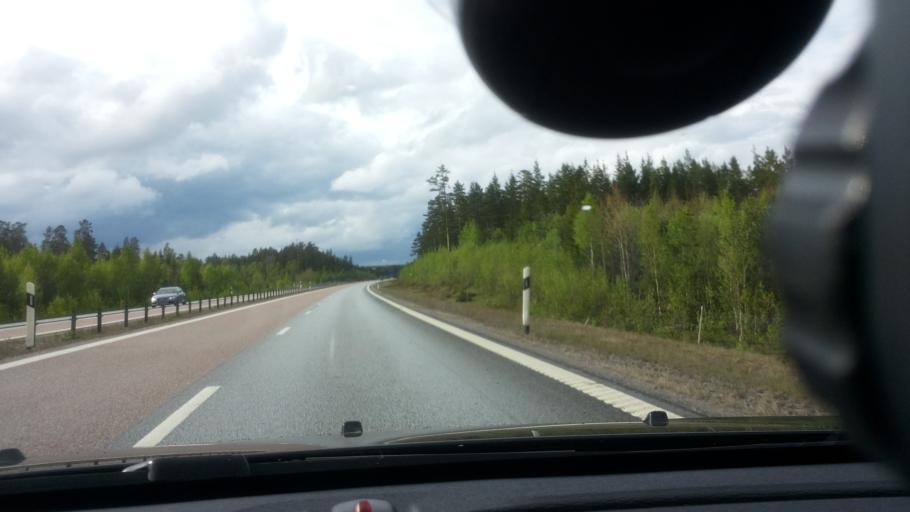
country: SE
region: Gaevleborg
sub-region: Soderhamns Kommun
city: Soderhamn
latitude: 61.4137
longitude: 16.9903
